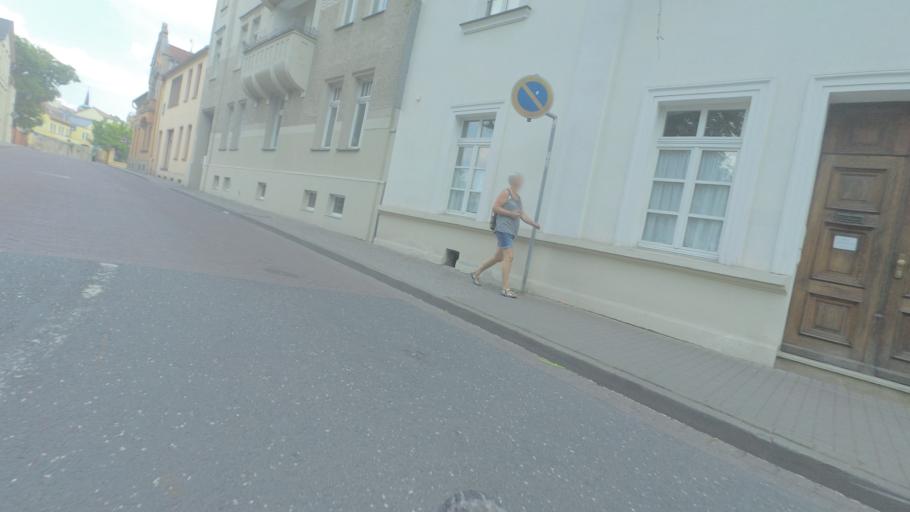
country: DE
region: Saxony-Anhalt
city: Koethen
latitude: 51.7503
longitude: 11.9693
